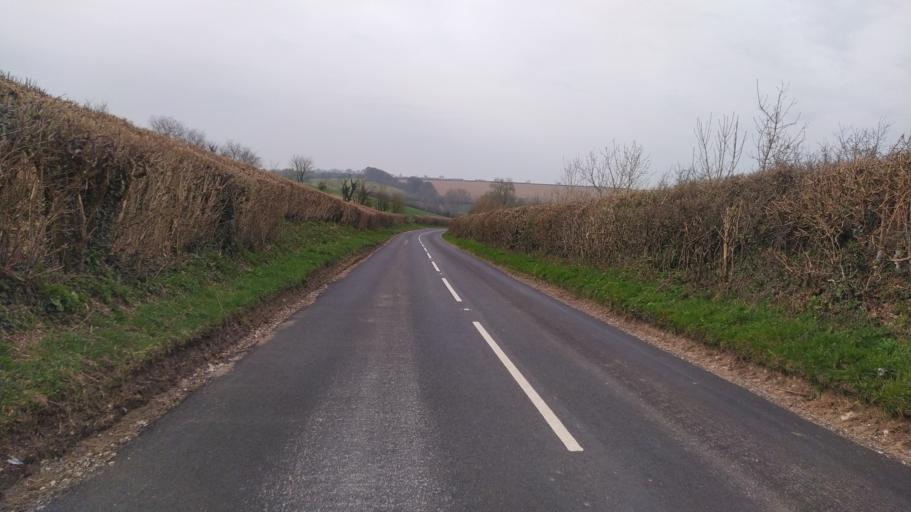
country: GB
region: England
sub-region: Dorset
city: Beaminster
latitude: 50.8194
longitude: -2.6847
